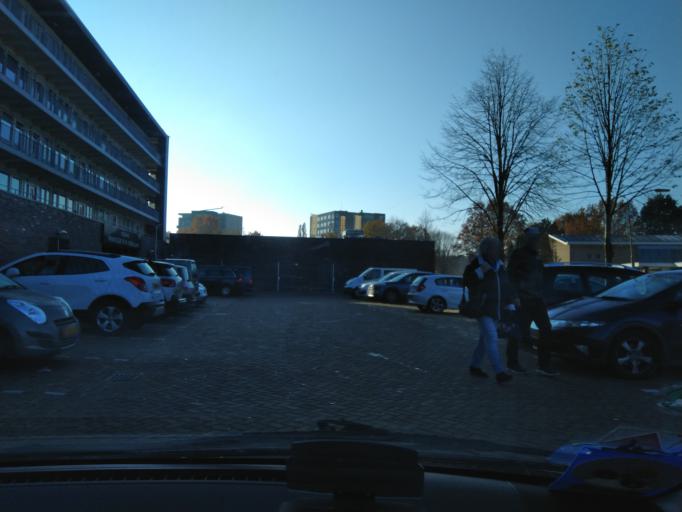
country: NL
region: Drenthe
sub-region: Gemeente Assen
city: Assen
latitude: 53.0011
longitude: 6.5481
